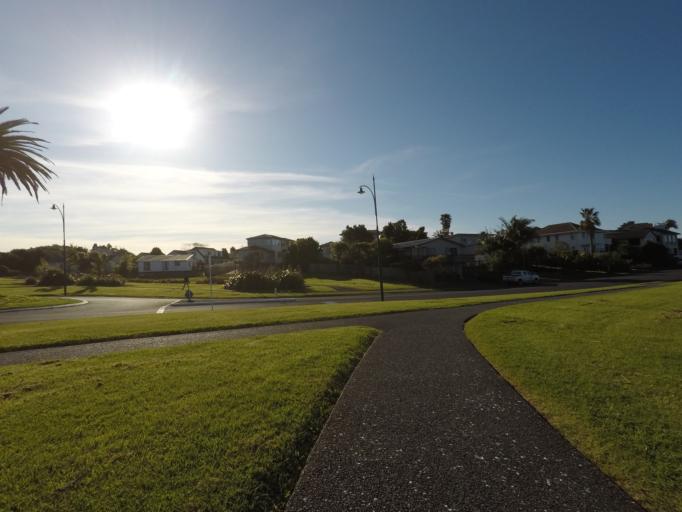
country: NZ
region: Auckland
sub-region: Auckland
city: Rosebank
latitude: -36.8340
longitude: 174.6607
